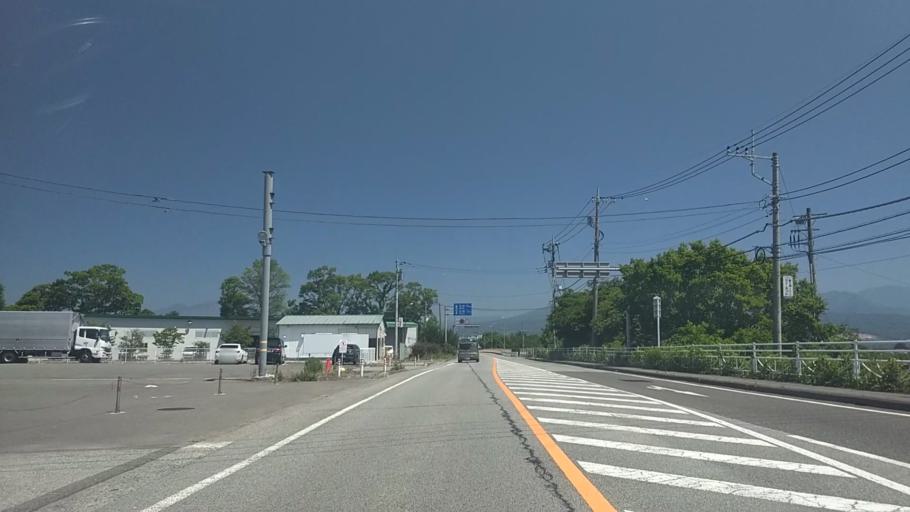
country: JP
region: Yamanashi
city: Nirasaki
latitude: 35.6697
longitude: 138.4647
